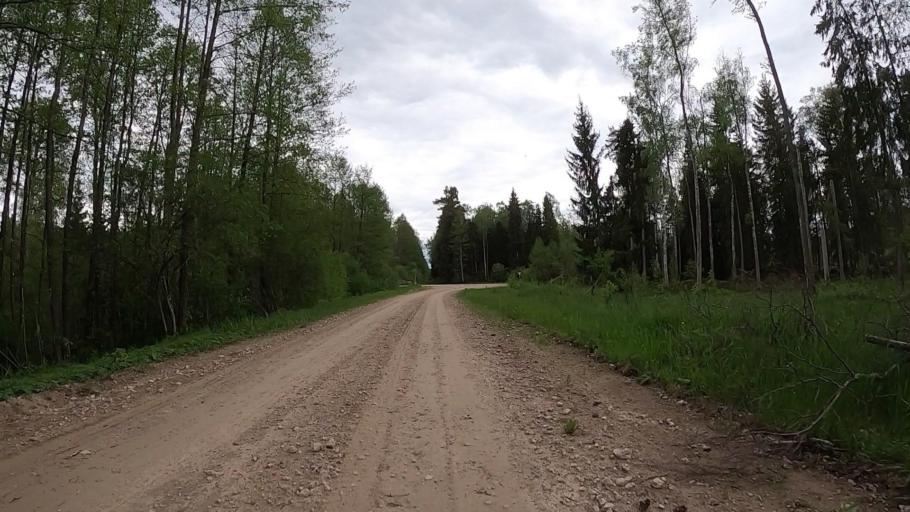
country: LV
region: Ozolnieku
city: Ozolnieki
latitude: 56.7743
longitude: 23.7670
